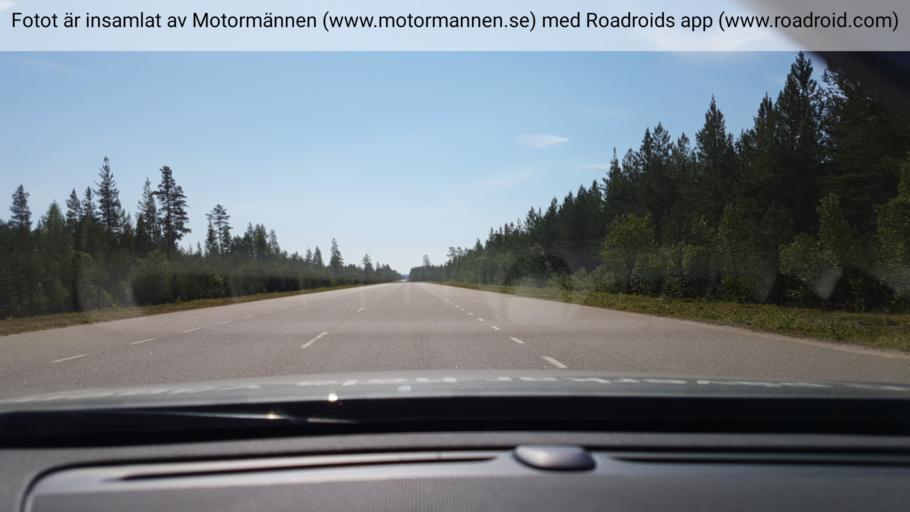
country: SE
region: Vaesterbotten
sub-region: Norsjo Kommun
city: Norsjoe
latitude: 64.5702
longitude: 19.3111
